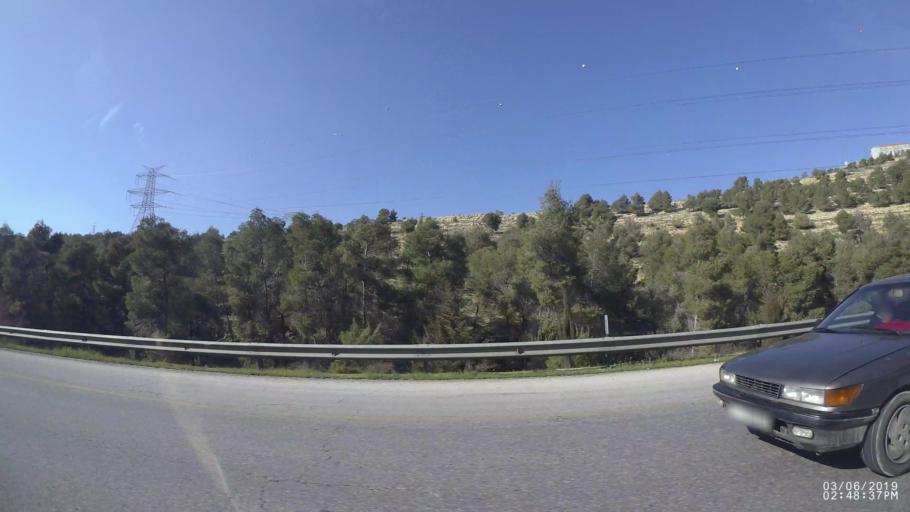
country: JO
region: Amman
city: Amman
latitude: 32.0249
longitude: 35.9550
